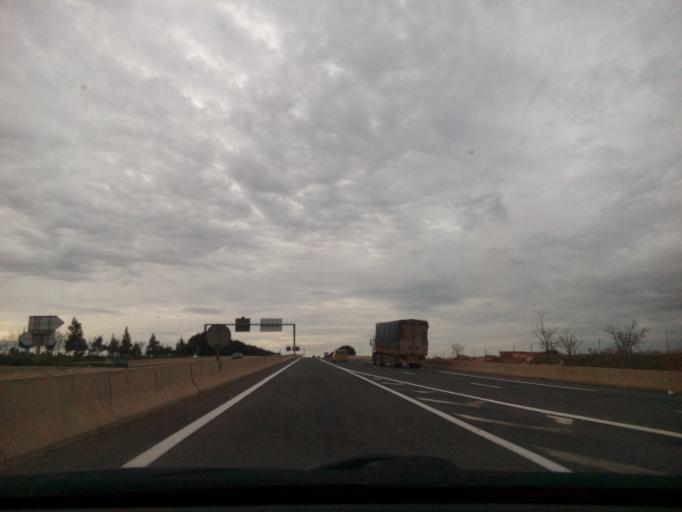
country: DZ
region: Mascara
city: Sig
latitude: 35.5420
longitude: -0.3449
